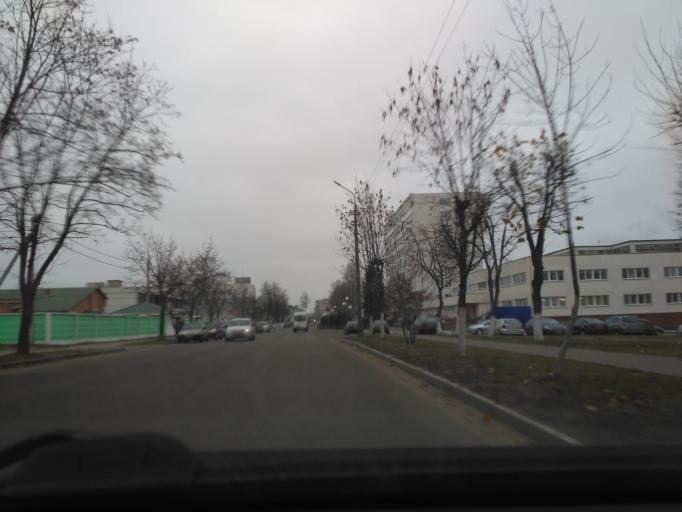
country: BY
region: Minsk
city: Horad Barysaw
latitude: 54.2112
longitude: 28.4905
